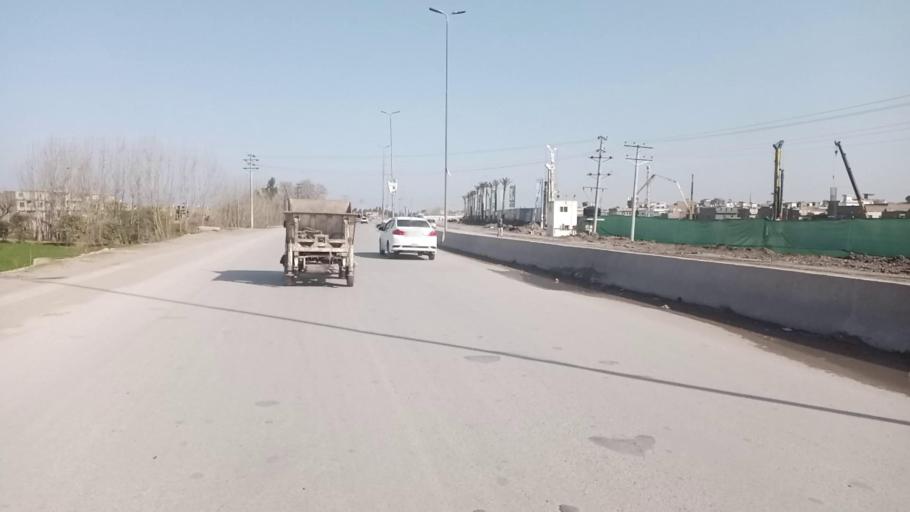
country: PK
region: Khyber Pakhtunkhwa
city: Peshawar
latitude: 34.0342
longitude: 71.5610
